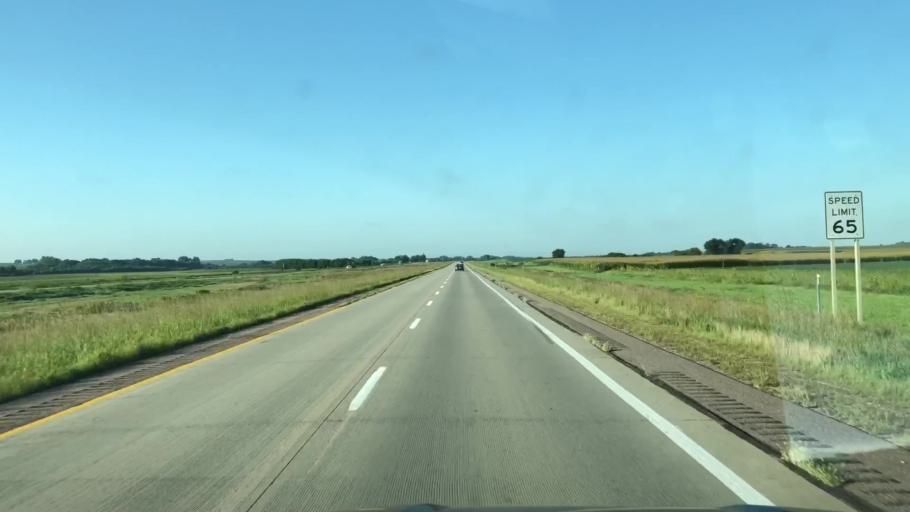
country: US
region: Iowa
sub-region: Sioux County
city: Orange City
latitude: 42.8930
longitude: -96.0917
